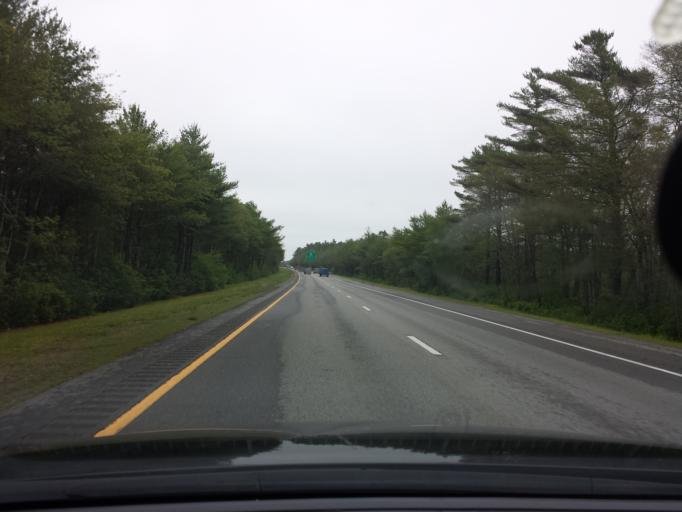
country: US
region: Massachusetts
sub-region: Plymouth County
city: Marion Center
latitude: 41.7146
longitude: -70.7868
